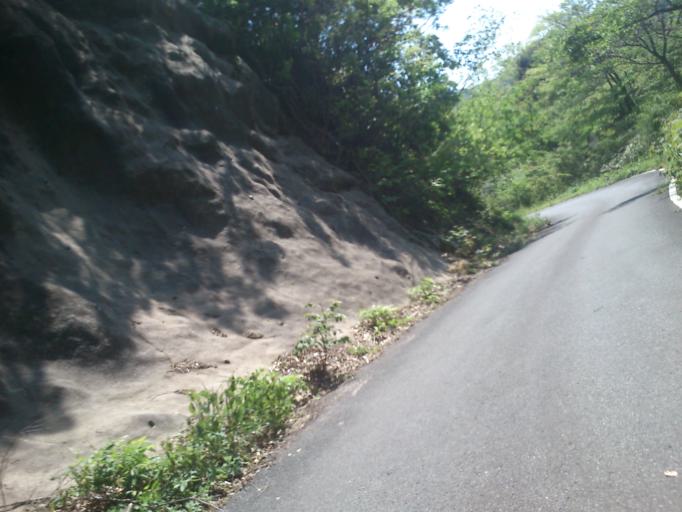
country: JP
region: Kyoto
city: Miyazu
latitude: 35.7008
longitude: 135.1553
